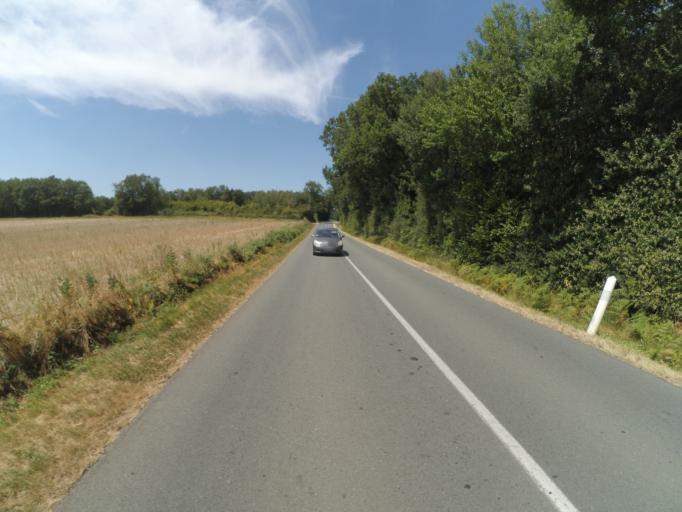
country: FR
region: Poitou-Charentes
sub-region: Departement de la Vienne
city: Saint-Maurice-la-Clouere
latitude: 46.3479
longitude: 0.4530
